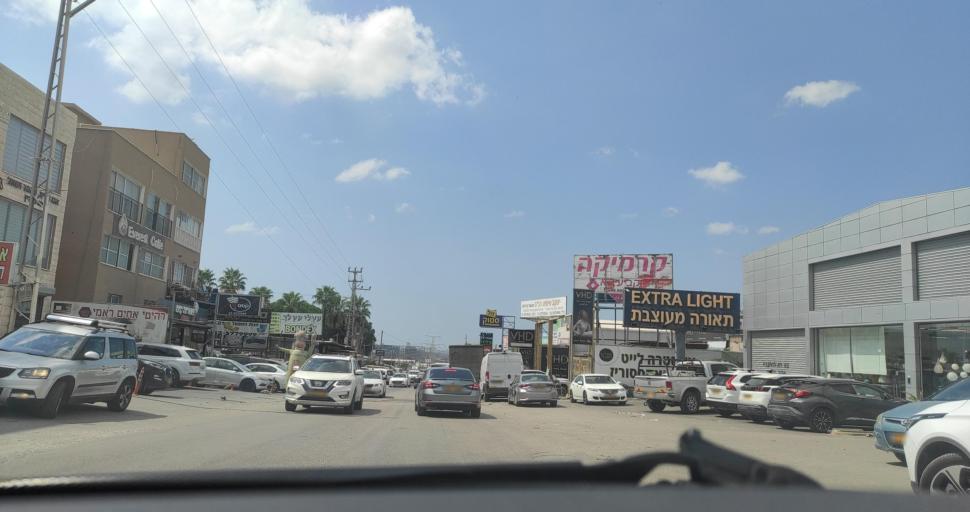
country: IL
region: Central District
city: Kafr Qasim
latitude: 32.1129
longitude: 34.9613
